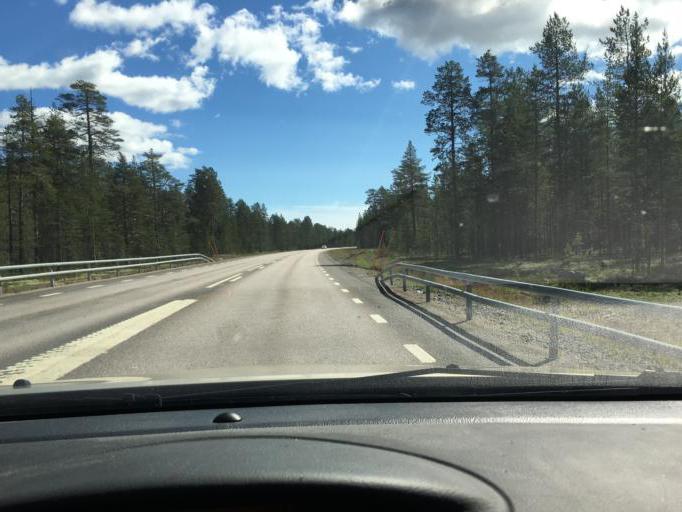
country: SE
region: Norrbotten
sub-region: Lulea Kommun
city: Bergnaset
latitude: 65.5661
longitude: 22.0860
